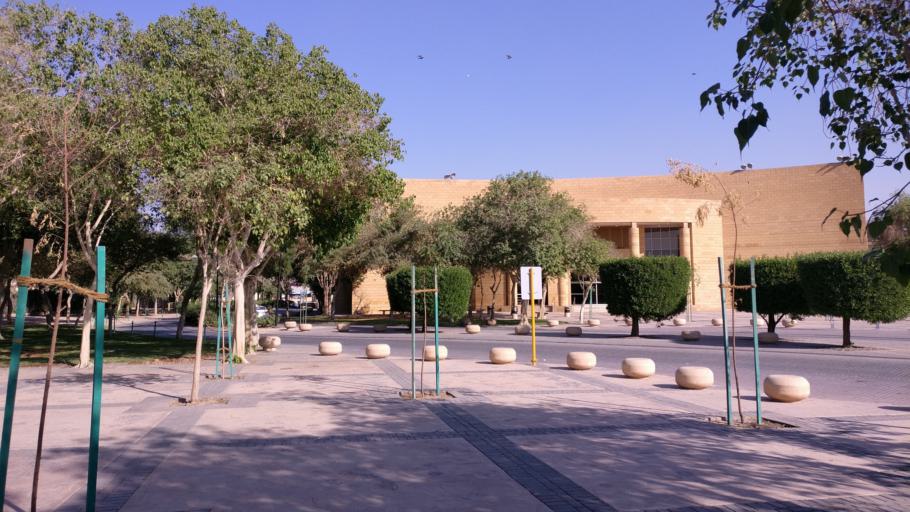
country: SA
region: Ar Riyad
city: Riyadh
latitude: 24.6439
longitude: 46.7105
